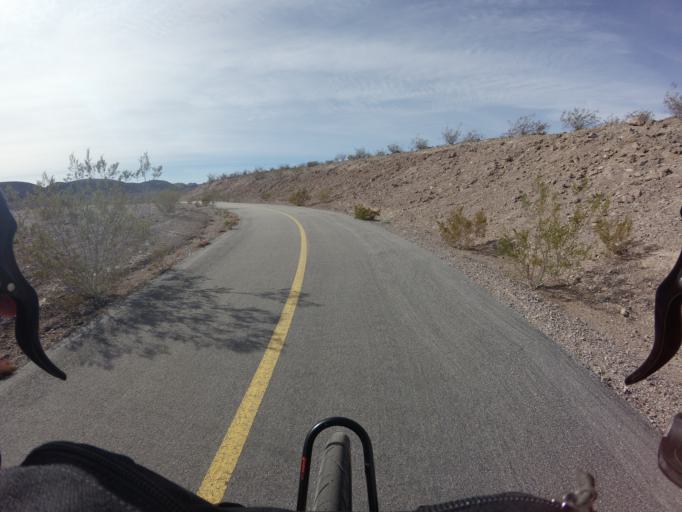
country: US
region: Nevada
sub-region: Clark County
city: Henderson
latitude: 36.1078
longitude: -114.8870
